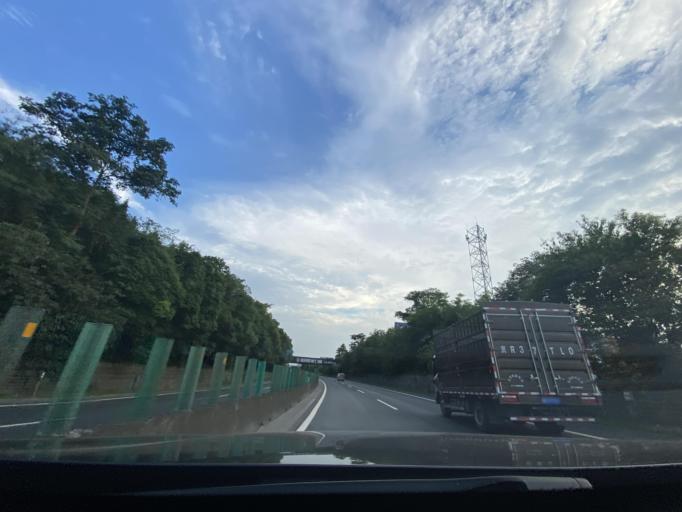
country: CN
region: Sichuan
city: Luojiang
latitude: 31.3894
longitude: 104.5555
